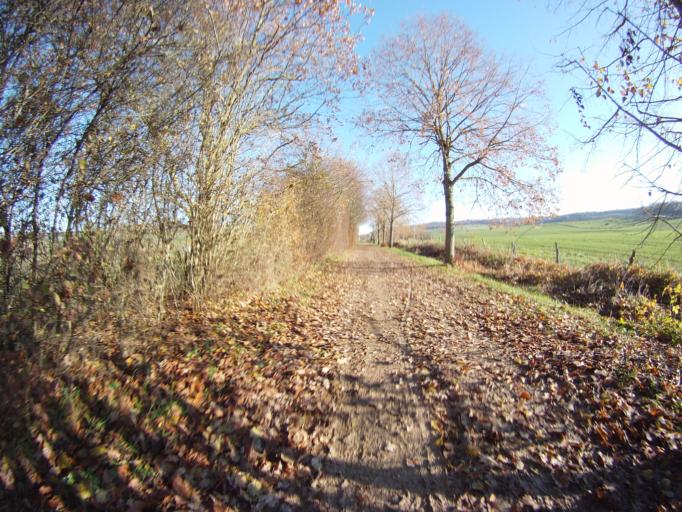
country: FR
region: Lorraine
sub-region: Departement de Meurthe-et-Moselle
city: Faulx
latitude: 48.7922
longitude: 6.2112
